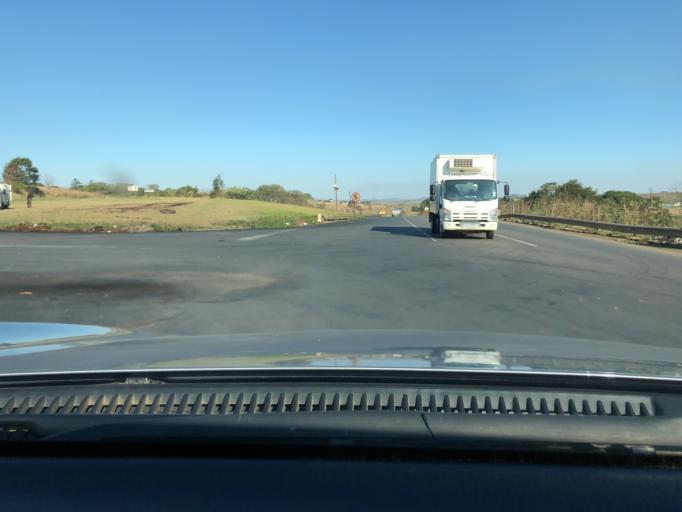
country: ZA
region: KwaZulu-Natal
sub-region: uMgungundlovu District Municipality
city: Camperdown
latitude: -29.7336
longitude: 30.5071
